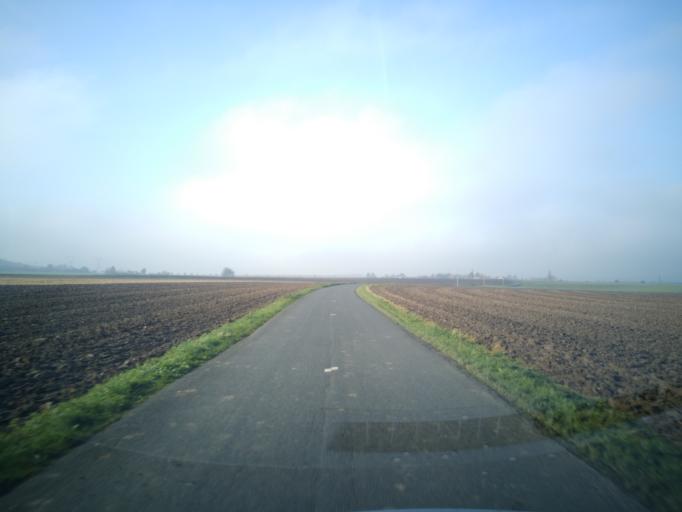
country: FR
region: Ile-de-France
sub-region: Departement des Yvelines
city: Saint-Germain-de-la-Grange
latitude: 48.8300
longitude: 1.9140
